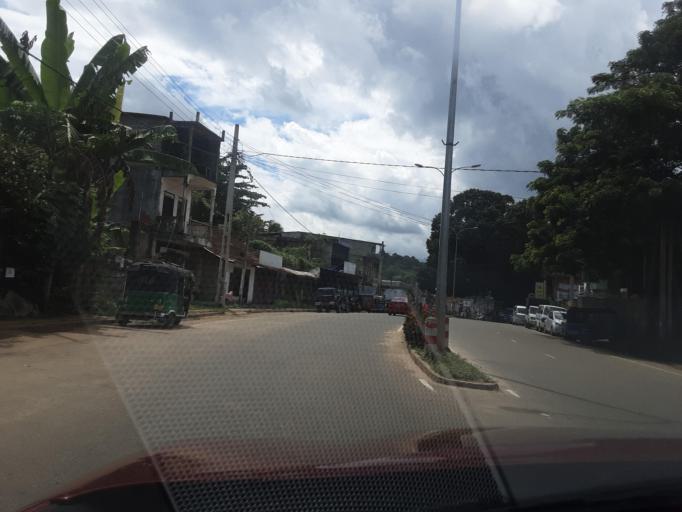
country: LK
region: Uva
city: Monaragala
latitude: 6.8958
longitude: 81.2381
